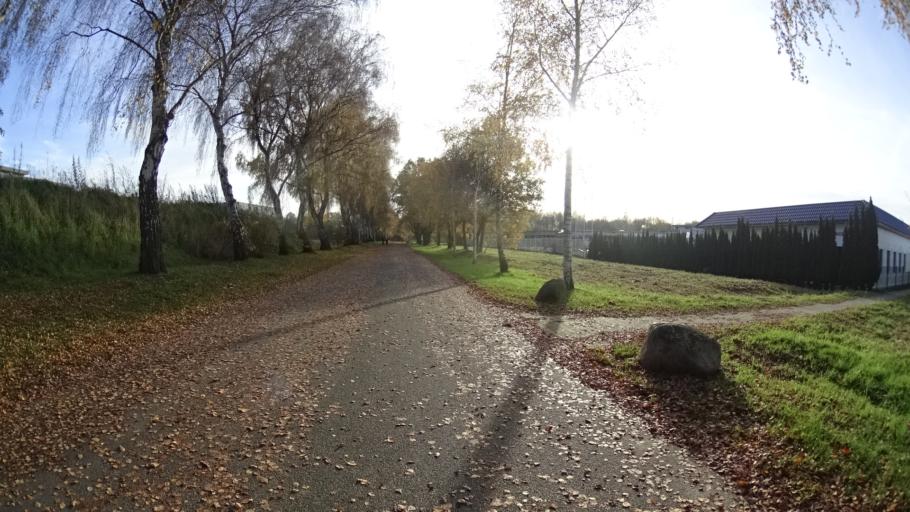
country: DE
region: Lower Saxony
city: Wendisch Evern
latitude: 53.2370
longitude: 10.4591
